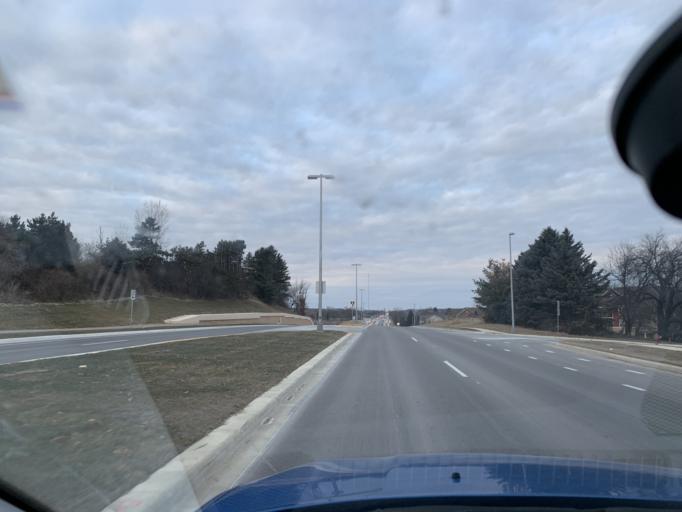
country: US
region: Wisconsin
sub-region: Dane County
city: Verona
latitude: 43.0055
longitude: -89.5335
